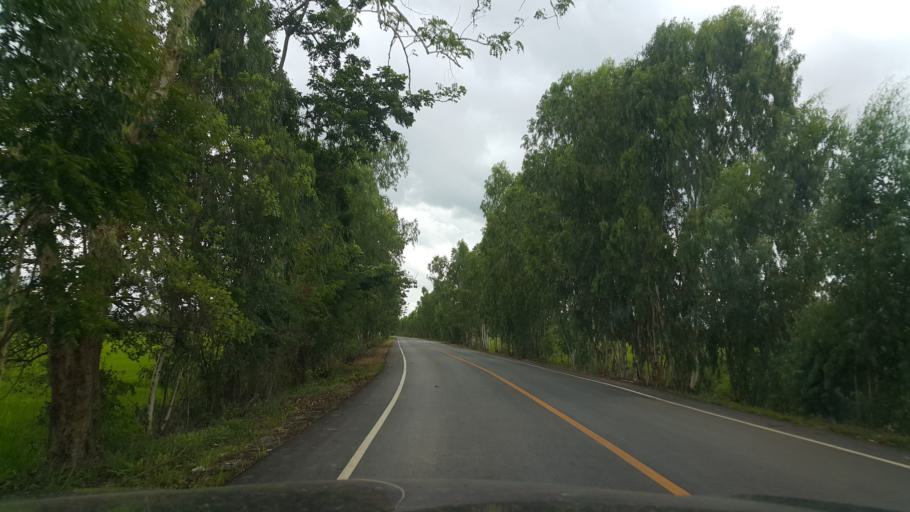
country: TH
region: Sukhothai
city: Kong Krailat
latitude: 16.9178
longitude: 99.8870
